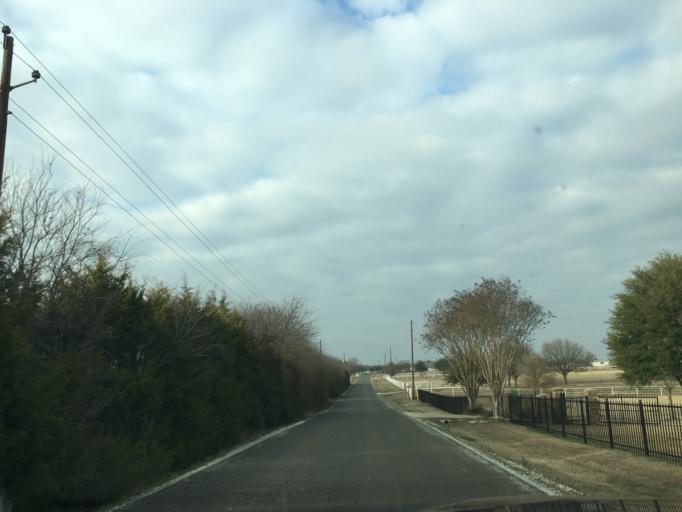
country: US
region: Texas
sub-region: Ellis County
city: Red Oak
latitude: 32.4810
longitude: -96.7894
